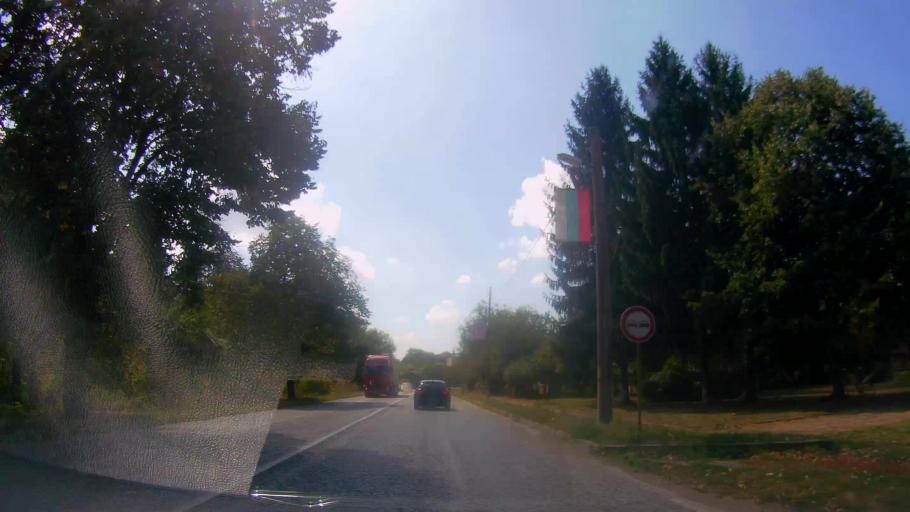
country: BG
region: Ruse
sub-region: Obshtina Borovo
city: Borovo
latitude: 43.5249
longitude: 25.7966
